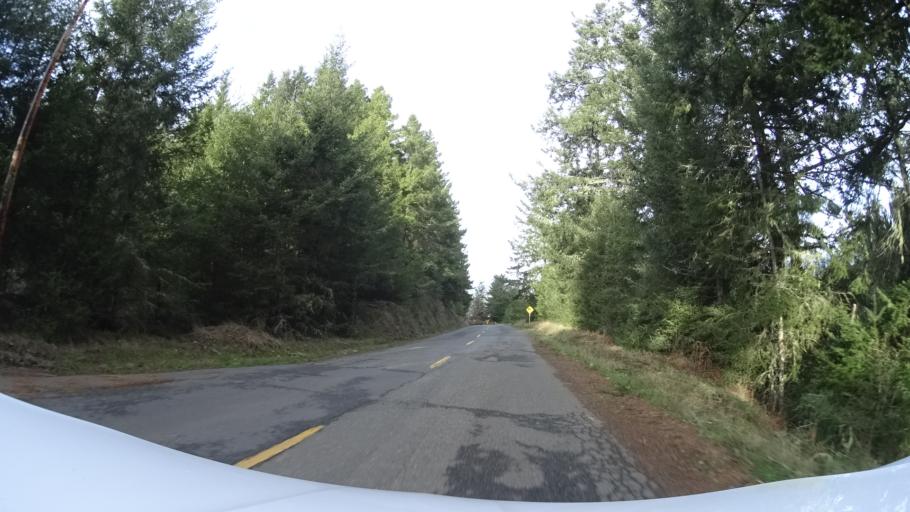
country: US
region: California
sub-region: Humboldt County
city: Ferndale
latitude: 40.5585
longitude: -124.2732
